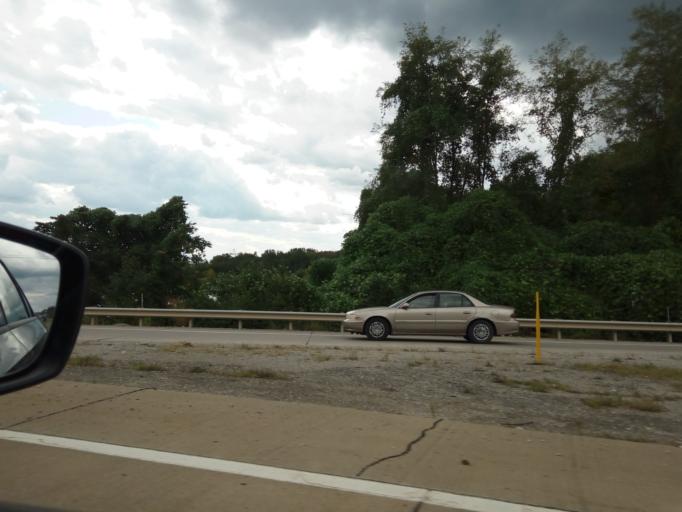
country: US
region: Kentucky
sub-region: Jefferson County
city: Anchorage
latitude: 38.2683
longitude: -85.5025
